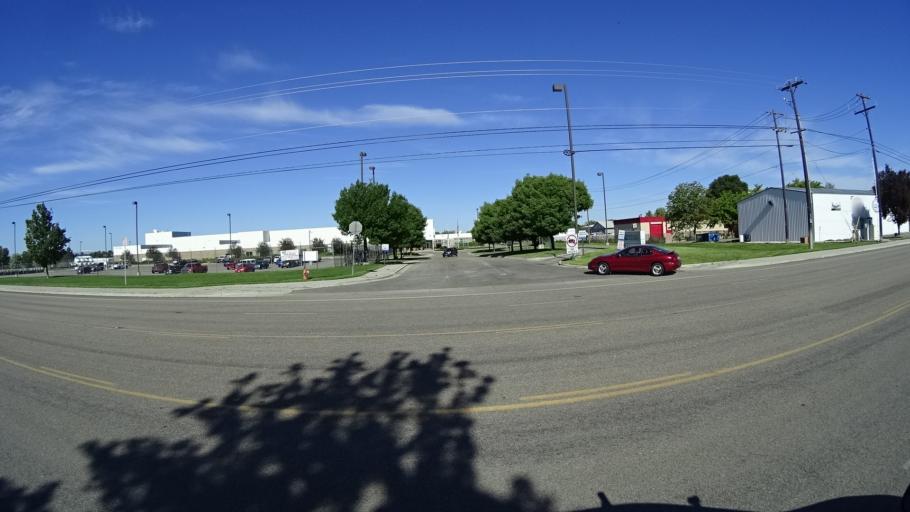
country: US
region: Idaho
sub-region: Ada County
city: Garden City
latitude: 43.5825
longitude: -116.2740
